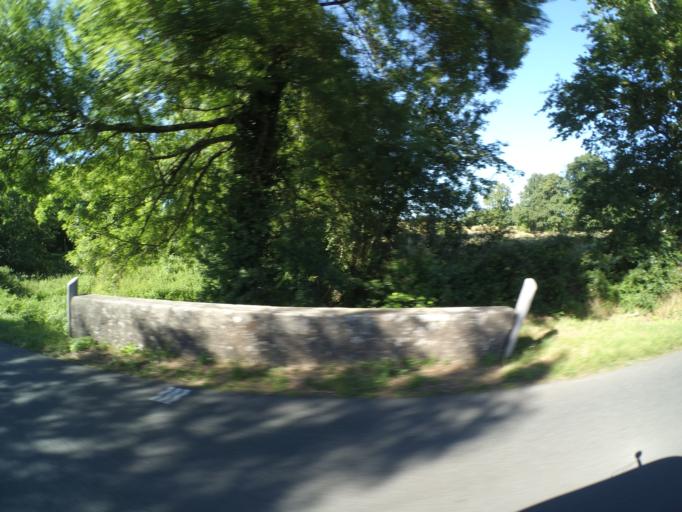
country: FR
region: Pays de la Loire
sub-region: Departement de la Vendee
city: Beaurepaire
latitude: 46.8970
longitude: -1.0642
